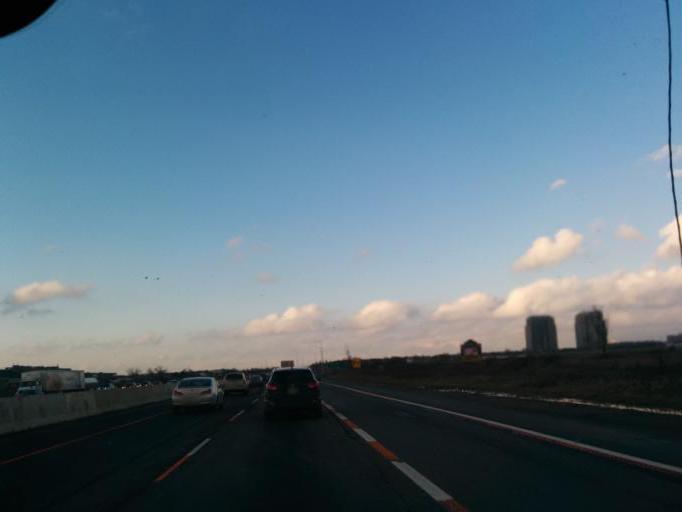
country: CA
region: Ontario
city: Etobicoke
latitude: 43.7127
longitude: -79.6167
